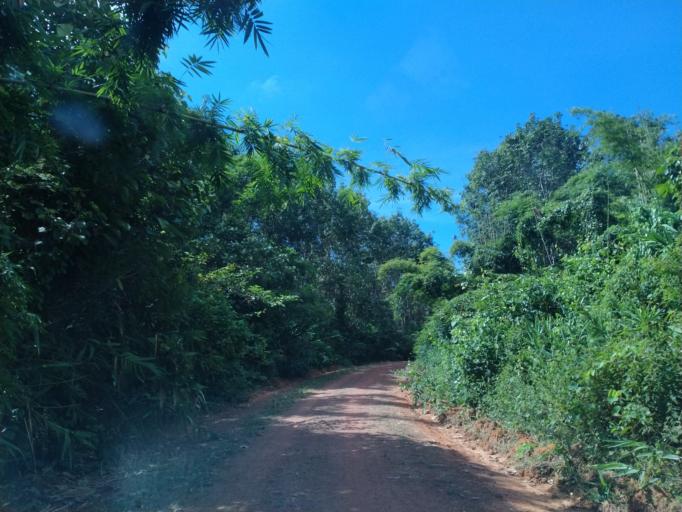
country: LA
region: Vientiane
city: Muang Phon-Hong
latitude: 18.6420
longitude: 102.8939
